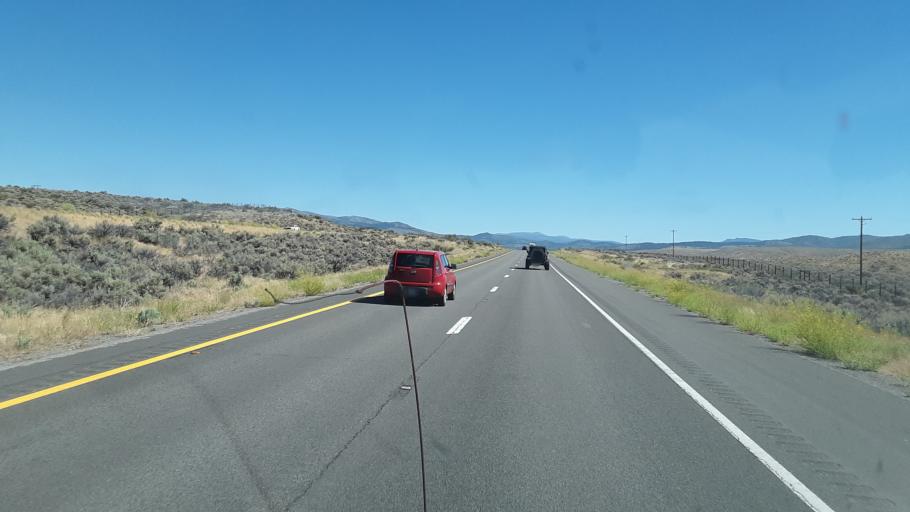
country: US
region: Nevada
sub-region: Washoe County
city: Cold Springs
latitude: 39.7158
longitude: -120.0375
